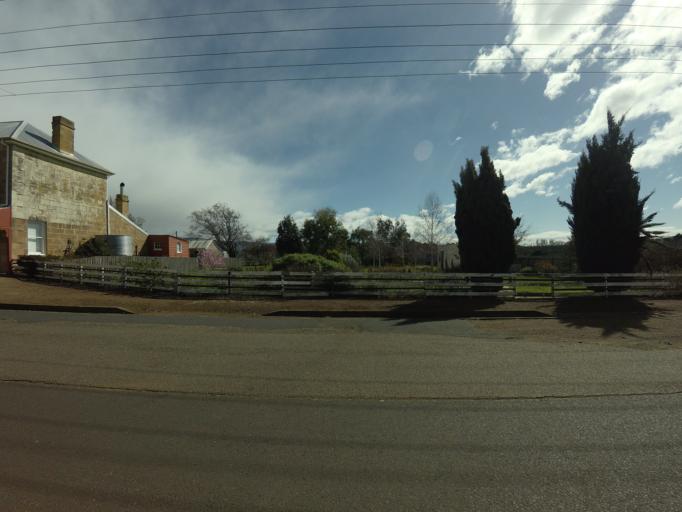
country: AU
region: Tasmania
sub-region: Northern Midlands
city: Evandale
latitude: -42.1417
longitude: 147.4226
